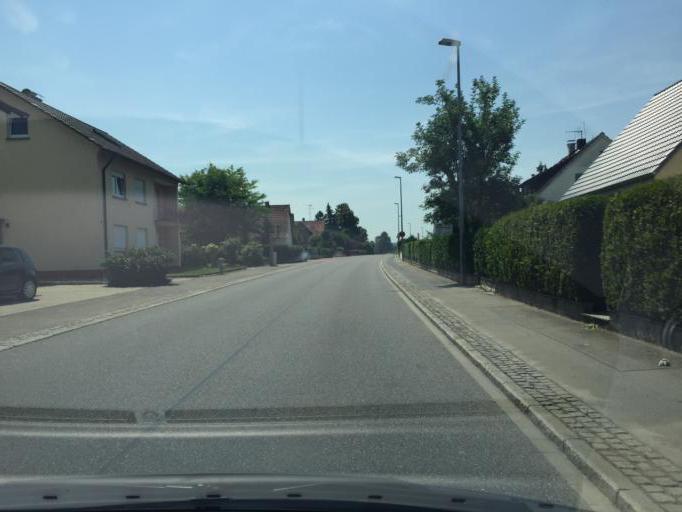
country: DE
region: Baden-Wuerttemberg
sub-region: Freiburg Region
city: Rielasingen-Worblingen
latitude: 47.7261
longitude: 8.8336
